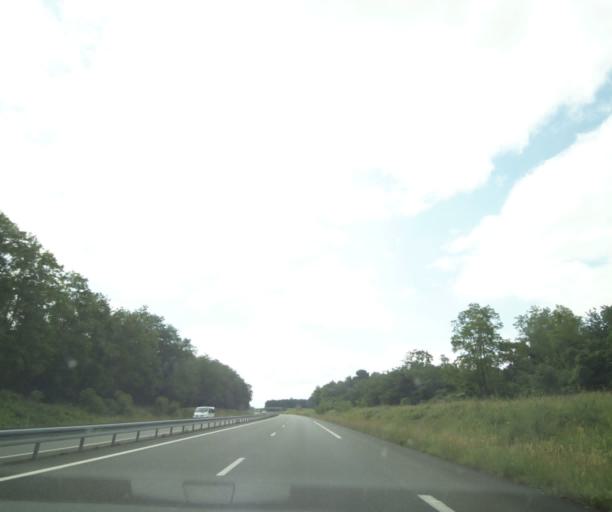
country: FR
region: Pays de la Loire
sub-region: Departement de Maine-et-Loire
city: Brion
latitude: 47.4335
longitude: -0.1653
